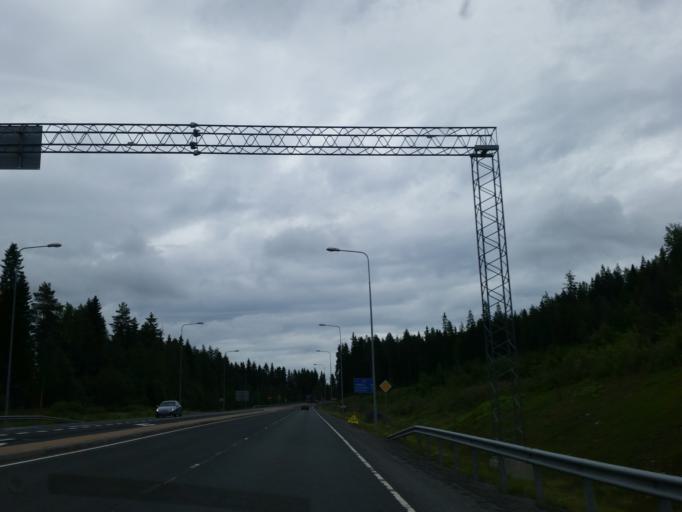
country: FI
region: Northern Savo
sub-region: Kuopio
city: Kuopio
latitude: 62.9757
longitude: 27.7124
